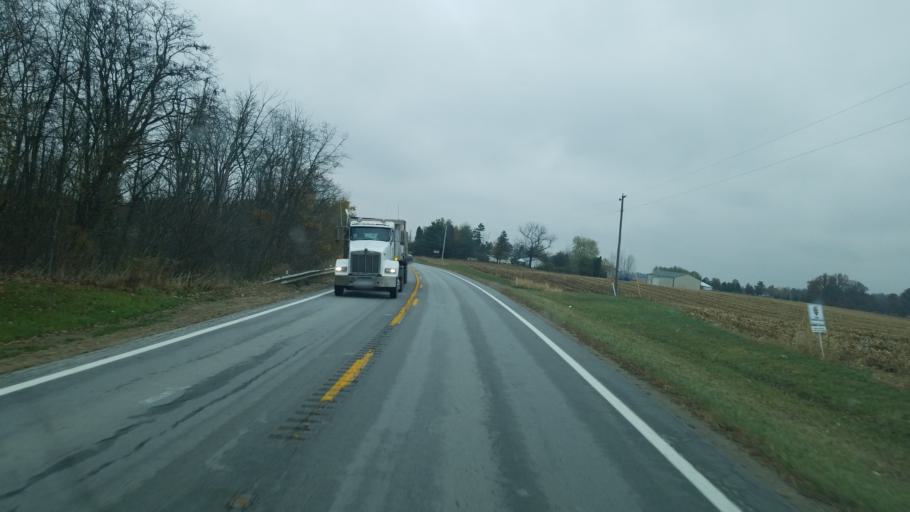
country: US
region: Ohio
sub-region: Union County
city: Marysville
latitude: 40.3093
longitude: -83.3305
